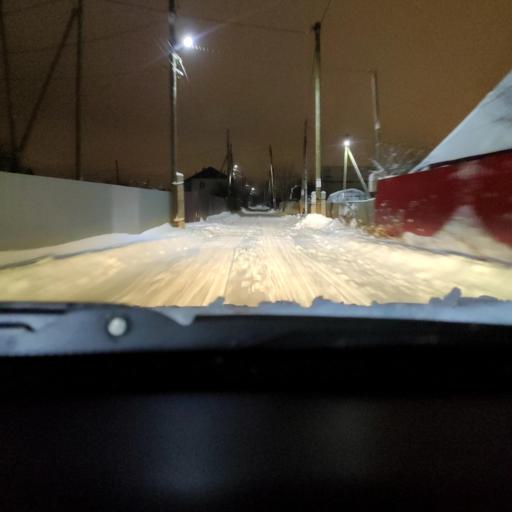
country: RU
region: Perm
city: Kondratovo
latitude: 57.9878
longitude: 56.1071
